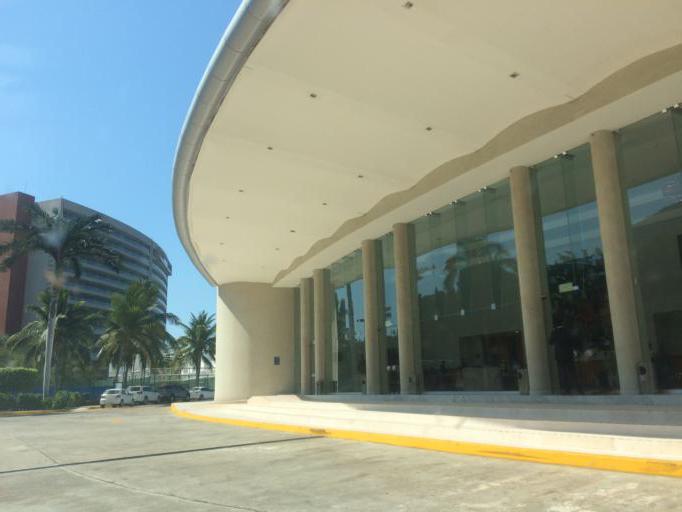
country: MX
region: Guerrero
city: Ixtapa
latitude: 17.6768
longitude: -101.6415
